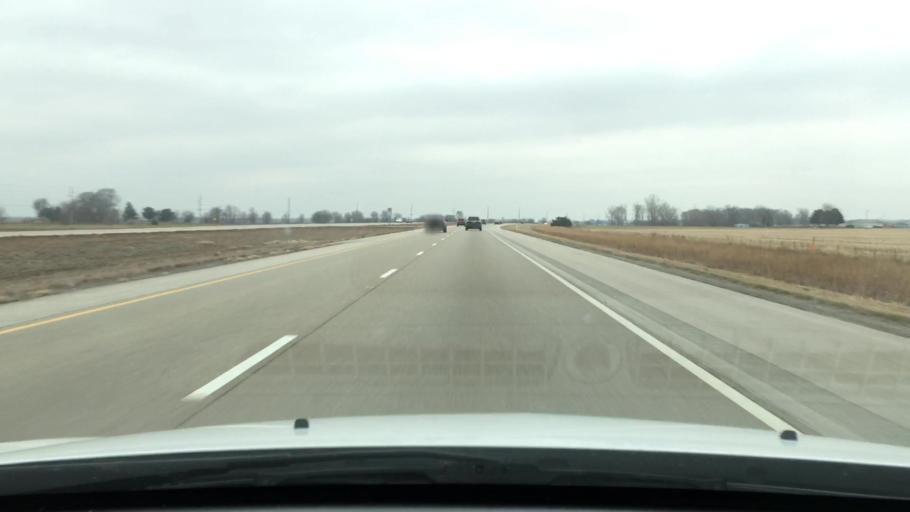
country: US
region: Illinois
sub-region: Logan County
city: Lincoln
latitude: 40.1939
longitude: -89.3055
